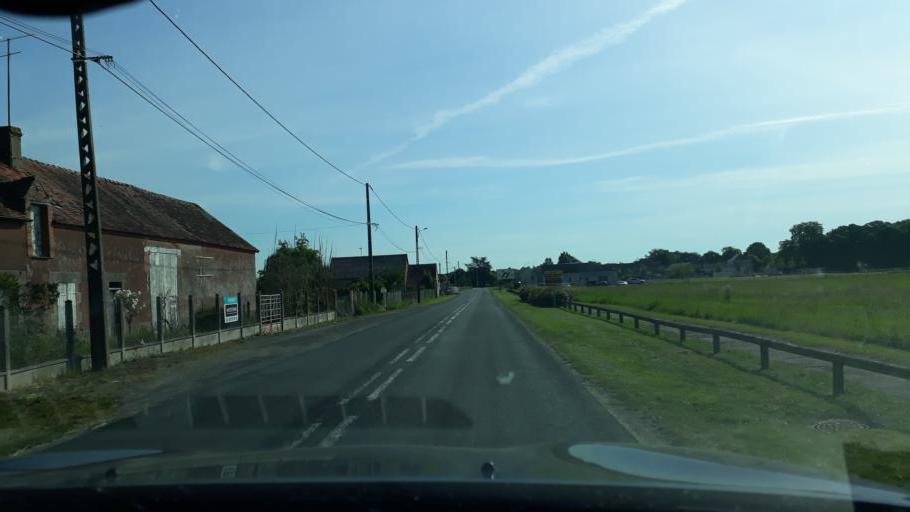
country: FR
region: Centre
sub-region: Departement du Loiret
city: Boynes
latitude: 48.0564
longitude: 2.2886
